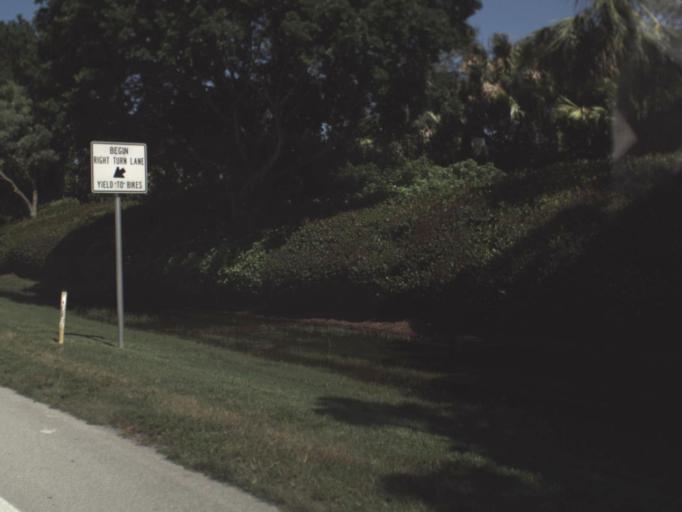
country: US
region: Florida
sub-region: Collier County
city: Naples Park
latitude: 26.2657
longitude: -81.8014
